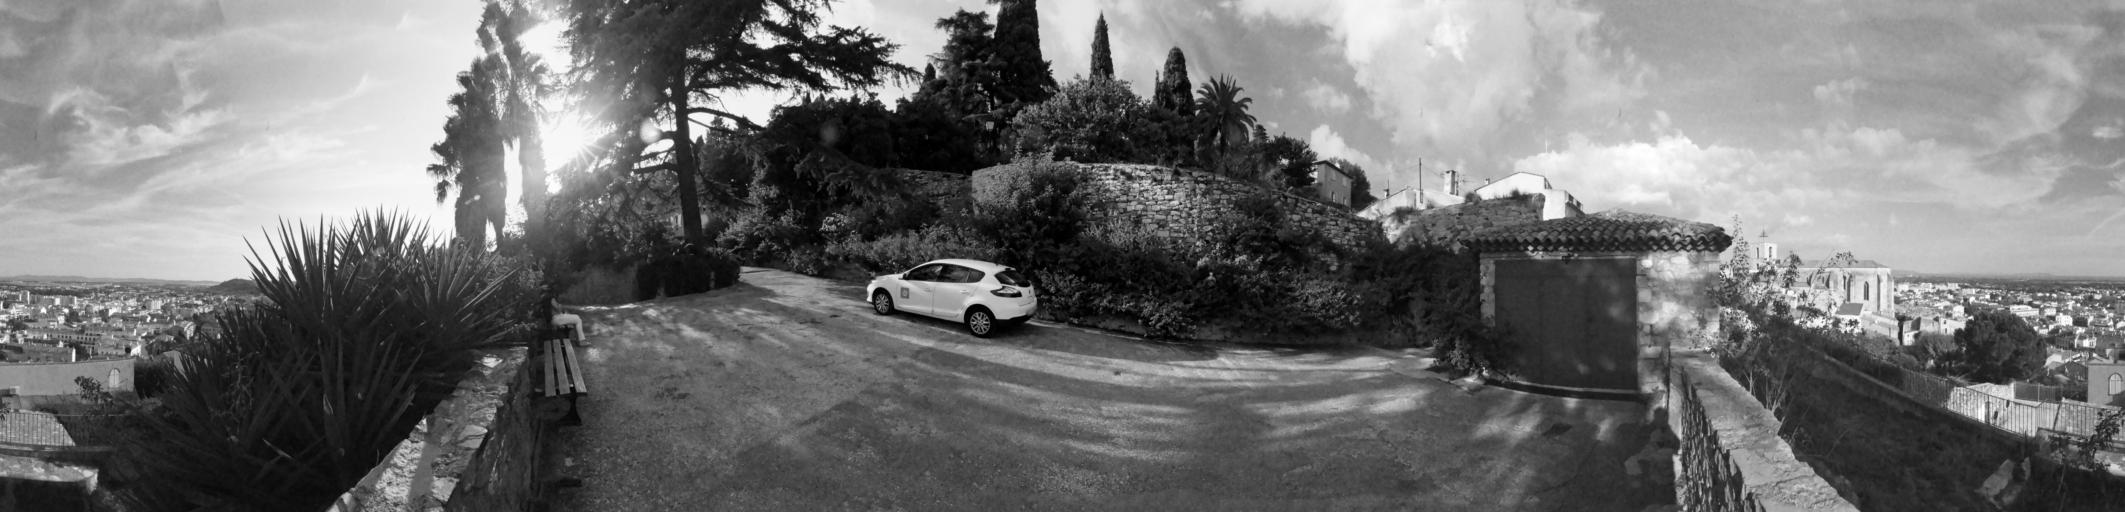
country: FR
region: Provence-Alpes-Cote d'Azur
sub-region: Departement du Var
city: Hyeres
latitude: 43.1214
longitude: 6.1255
